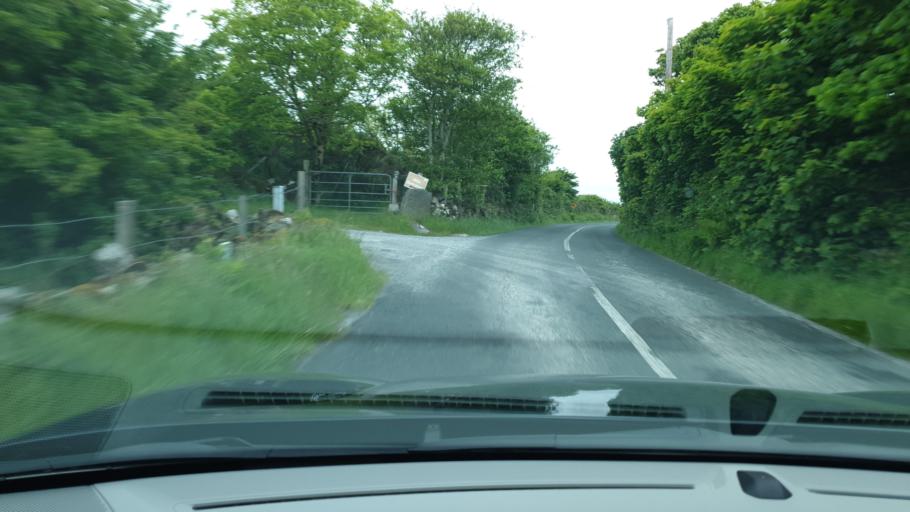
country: IE
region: Connaught
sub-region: County Galway
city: Clifden
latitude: 53.3897
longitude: -9.9783
